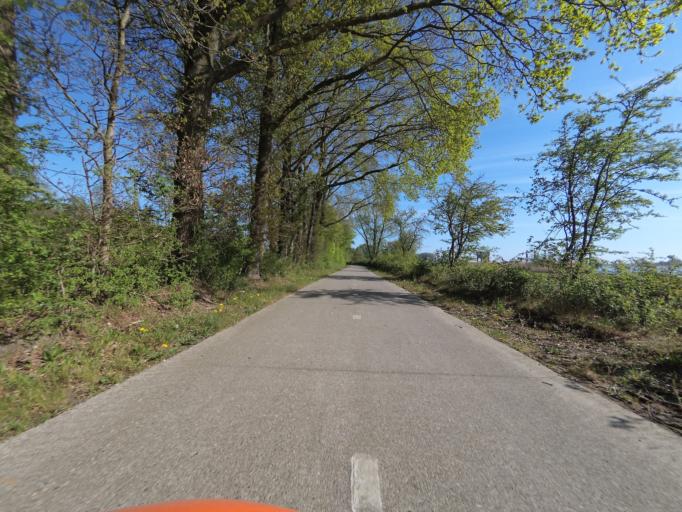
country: NL
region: Gelderland
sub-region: Gemeente Elburg
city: Elburg
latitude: 52.5148
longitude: 5.8541
